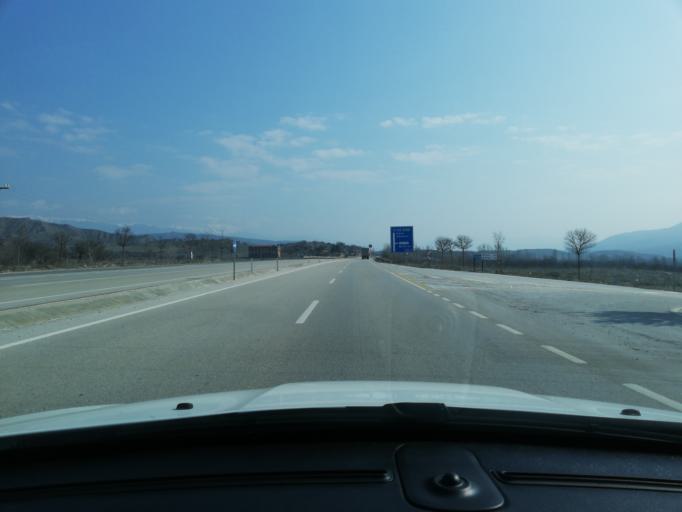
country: TR
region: Cankiri
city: Beloren
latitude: 40.8665
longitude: 33.4864
